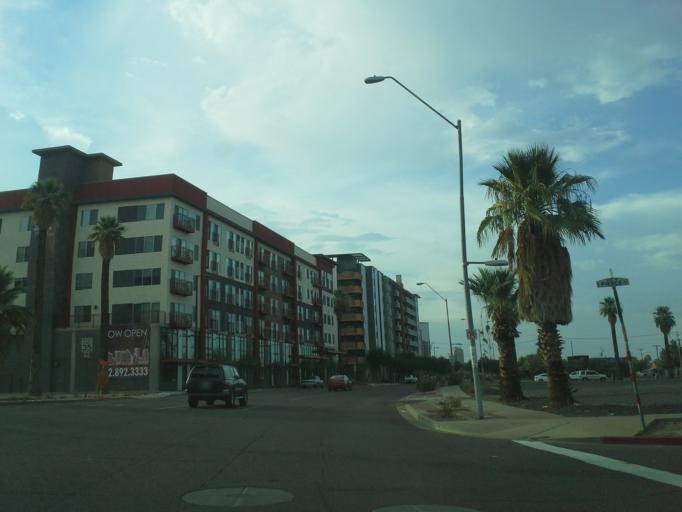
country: US
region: Arizona
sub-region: Maricopa County
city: Phoenix
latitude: 33.4554
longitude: -112.0685
